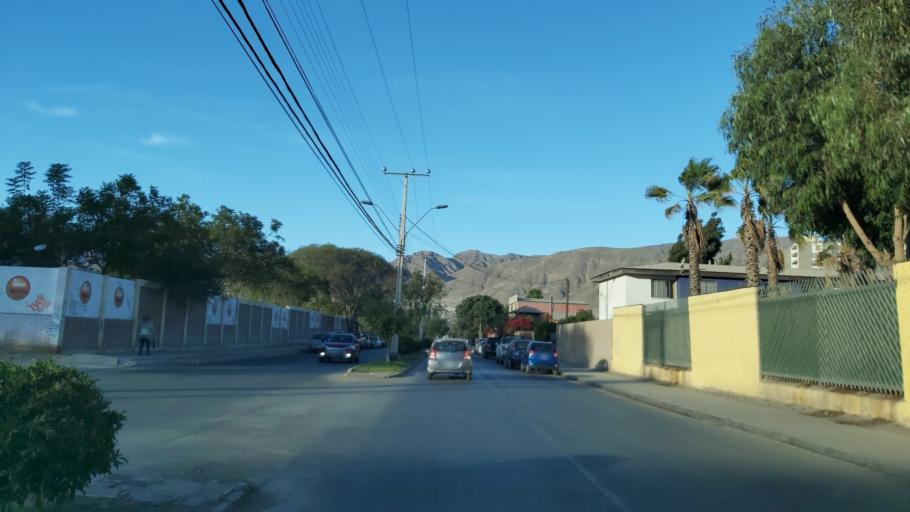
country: CL
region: Atacama
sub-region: Provincia de Copiapo
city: Copiapo
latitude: -27.3782
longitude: -70.3186
